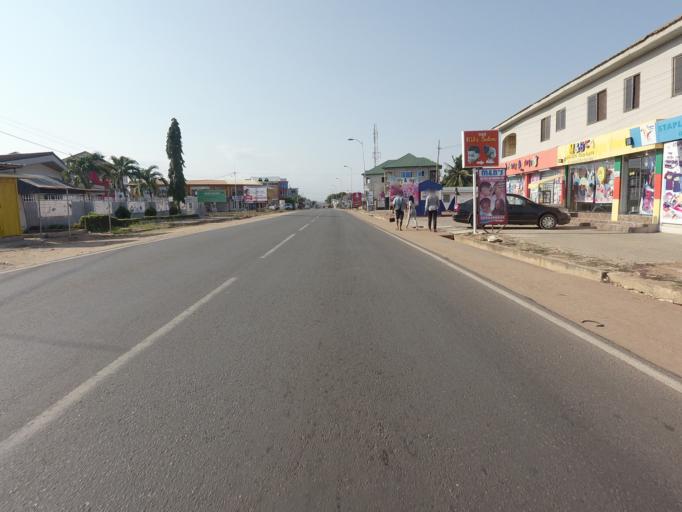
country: GH
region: Greater Accra
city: Nungua
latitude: 5.6316
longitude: -0.0762
